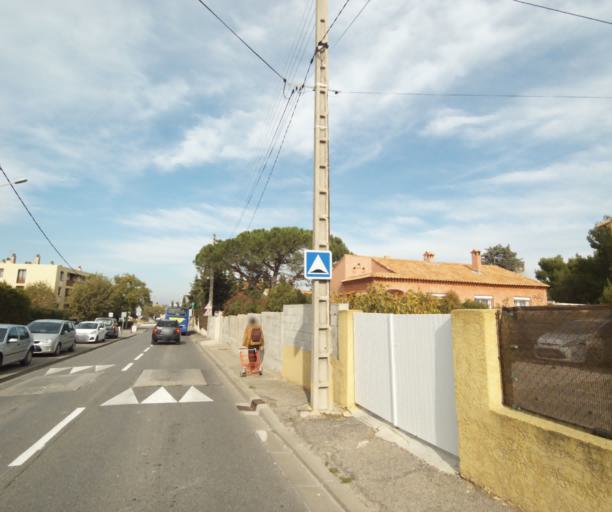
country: FR
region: Provence-Alpes-Cote d'Azur
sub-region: Departement des Bouches-du-Rhone
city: Gignac-la-Nerthe
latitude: 43.3930
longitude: 5.2318
